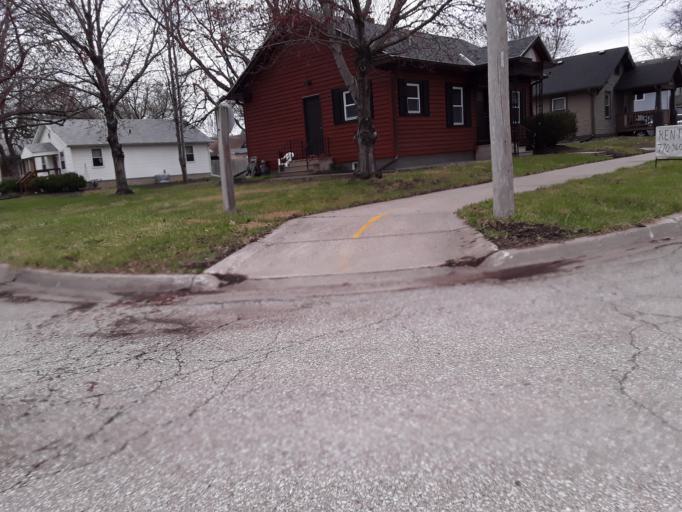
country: US
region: Nebraska
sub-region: Lancaster County
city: Lincoln
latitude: 40.8300
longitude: -96.6911
